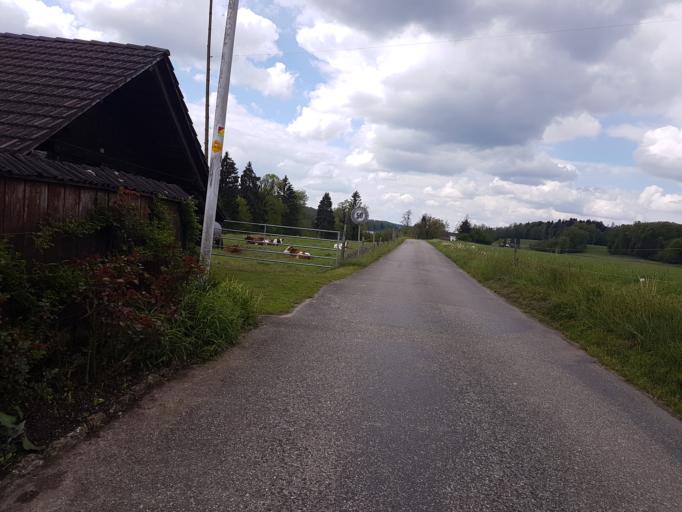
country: CH
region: Solothurn
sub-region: Bezirk Gaeu
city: Wolfwil
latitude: 47.2624
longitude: 7.7930
